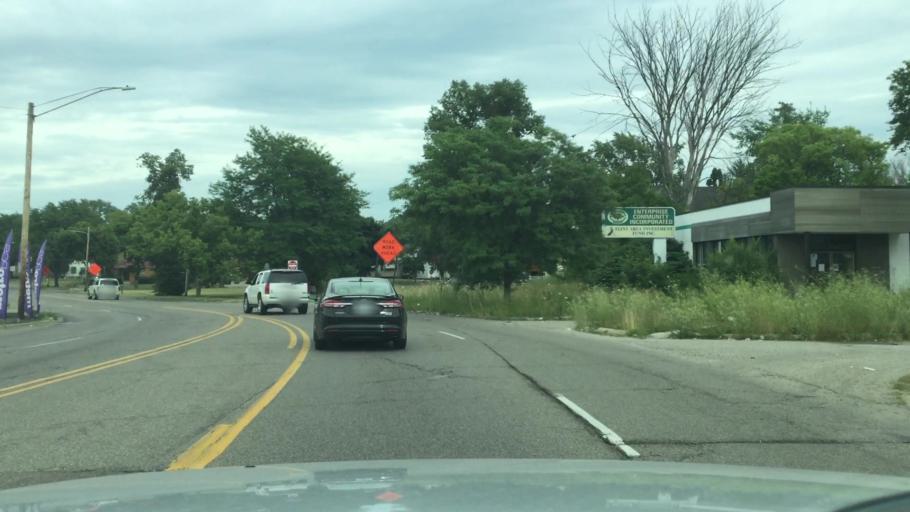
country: US
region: Michigan
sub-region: Genesee County
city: Flint
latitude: 43.0307
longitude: -83.7151
